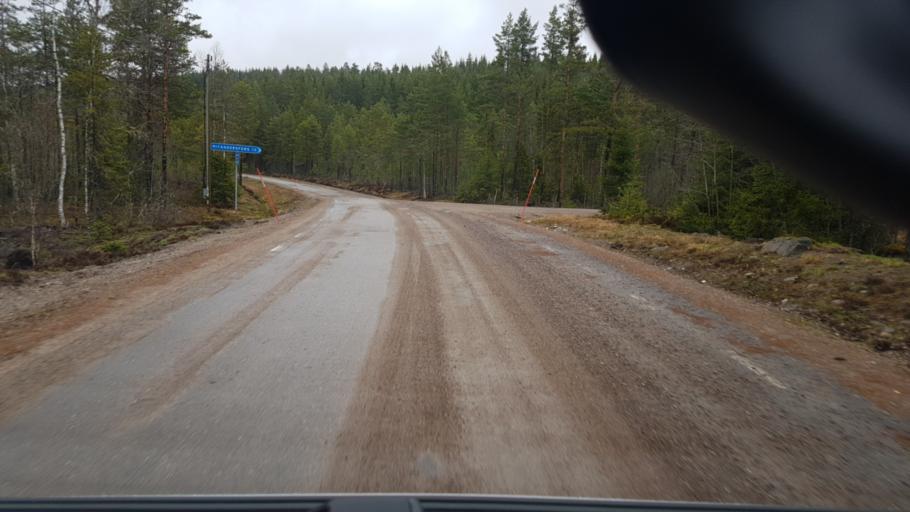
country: SE
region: Vaermland
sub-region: Eda Kommun
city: Charlottenberg
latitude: 59.9811
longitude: 12.4902
